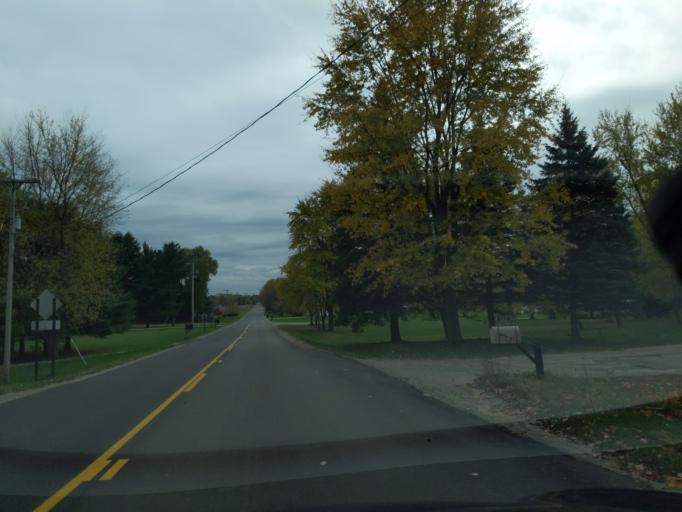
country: US
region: Michigan
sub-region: Eaton County
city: Eaton Rapids
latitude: 42.5370
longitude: -84.6213
